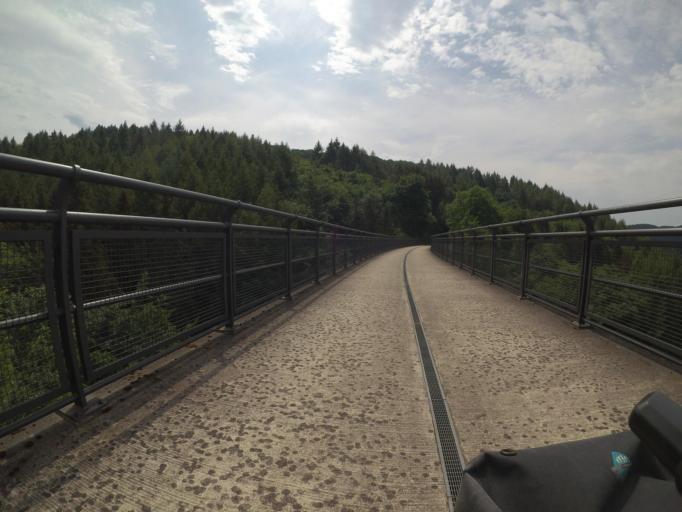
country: DE
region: Rheinland-Pfalz
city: Plein
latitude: 50.0219
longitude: 6.8761
